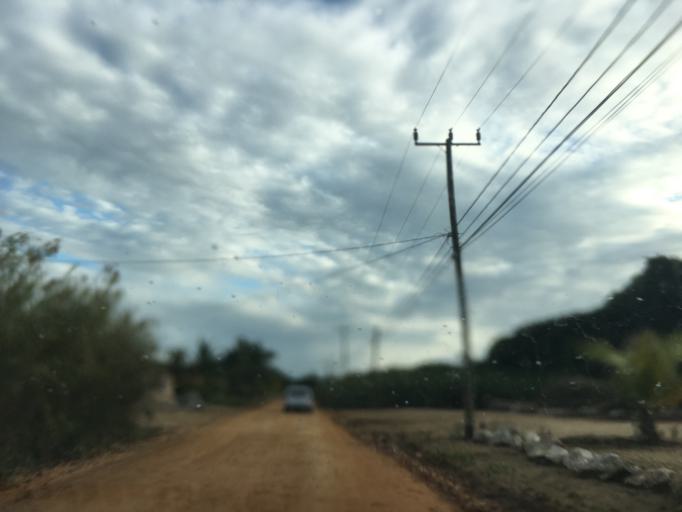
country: BZ
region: Stann Creek
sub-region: Dangriga
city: Dangriga
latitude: 16.8247
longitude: -88.2666
